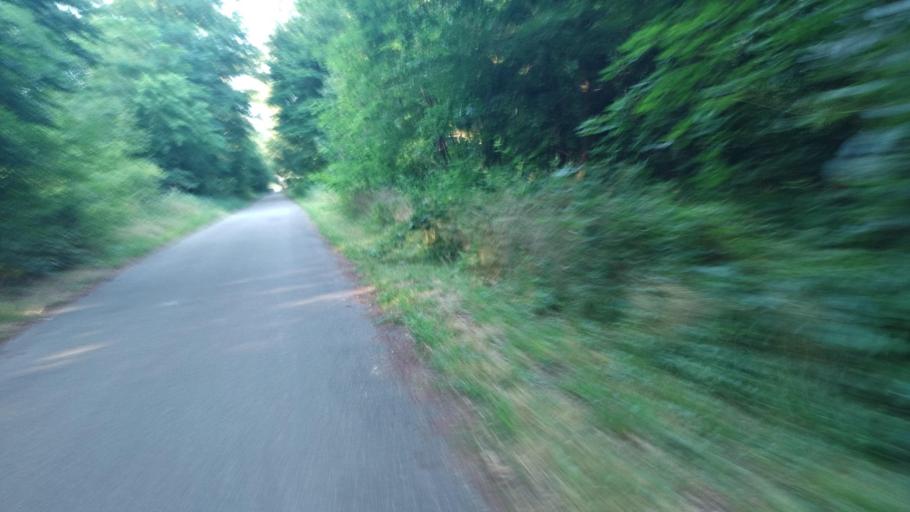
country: DE
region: Baden-Wuerttemberg
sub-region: Karlsruhe Region
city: Karlsruhe
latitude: 48.9750
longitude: 8.3849
